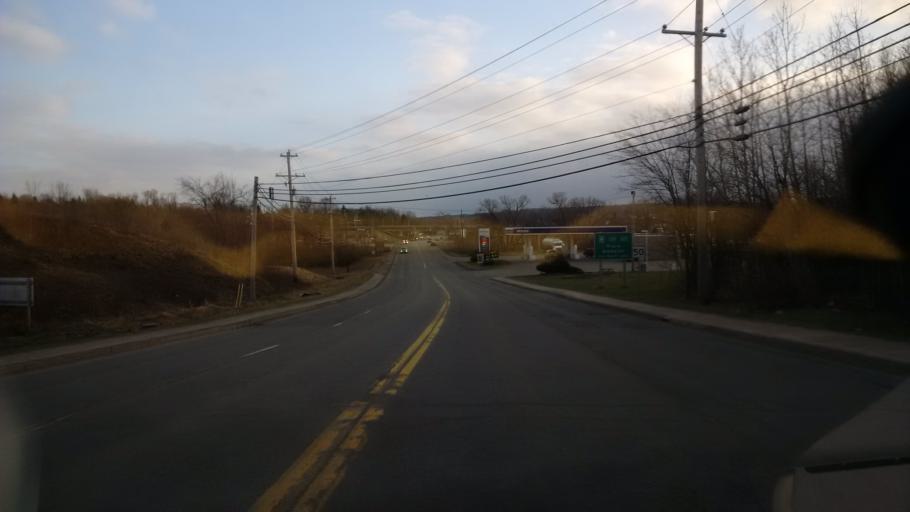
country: CA
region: Nova Scotia
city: New Glasgow
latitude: 45.5686
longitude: -62.6433
